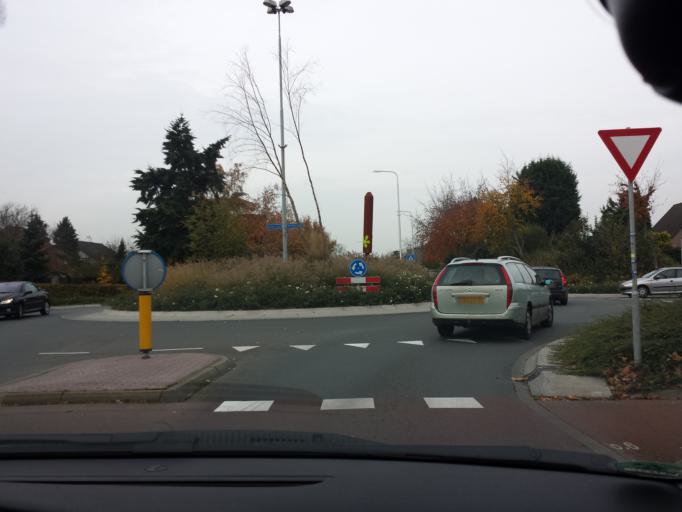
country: NL
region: North Brabant
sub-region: Gemeente Cuijk
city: Cuijk
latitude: 51.7760
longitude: 5.8577
